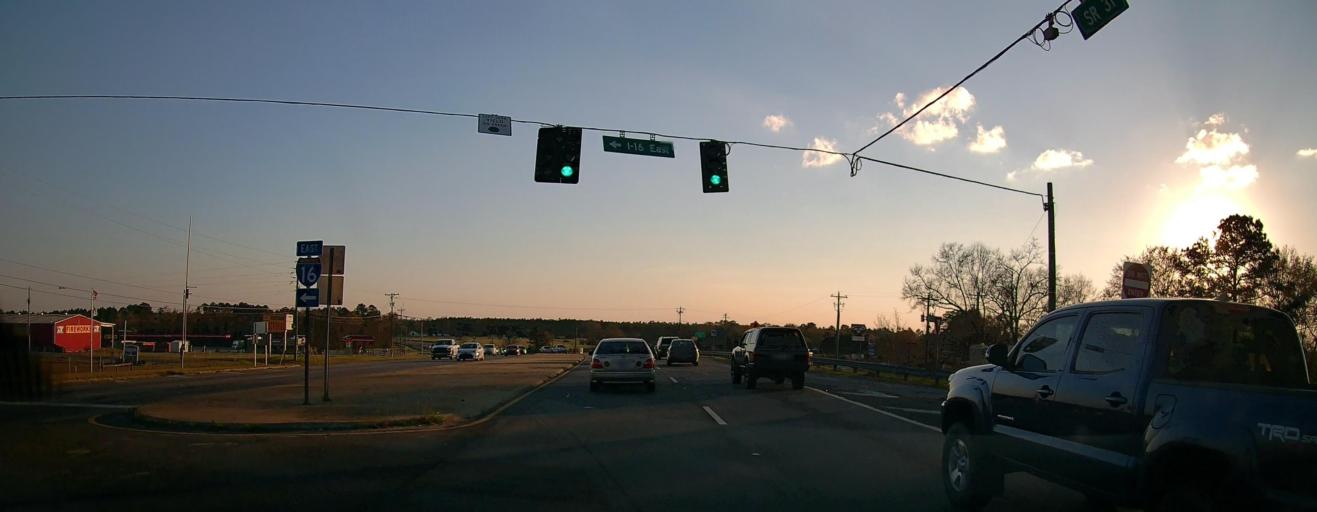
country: US
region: Georgia
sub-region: Laurens County
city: Dublin
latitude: 32.4872
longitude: -82.9358
